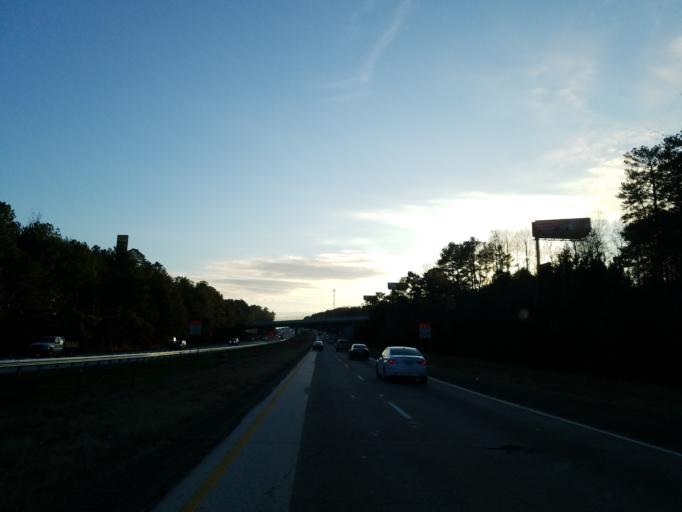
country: US
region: Georgia
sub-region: Forsyth County
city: Cumming
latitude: 34.1956
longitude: -84.1301
